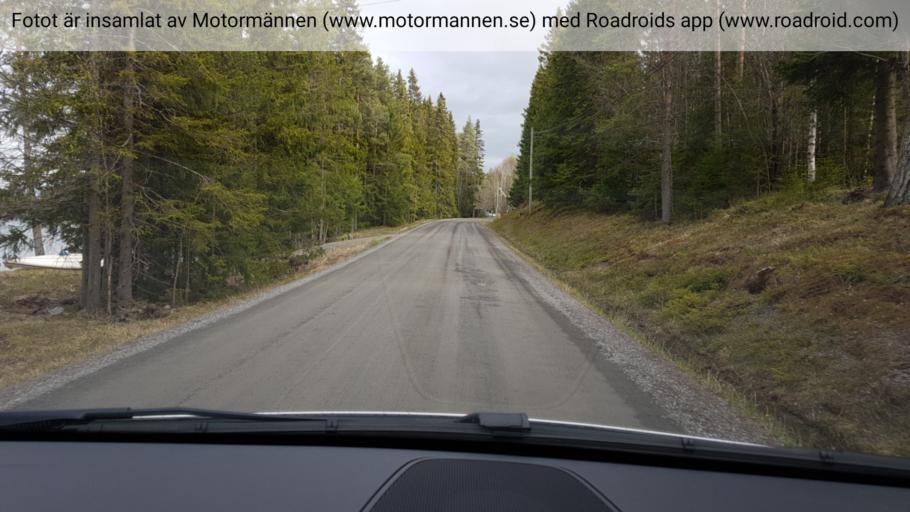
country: SE
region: Jaemtland
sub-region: OEstersunds Kommun
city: Brunflo
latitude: 63.0092
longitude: 14.7854
